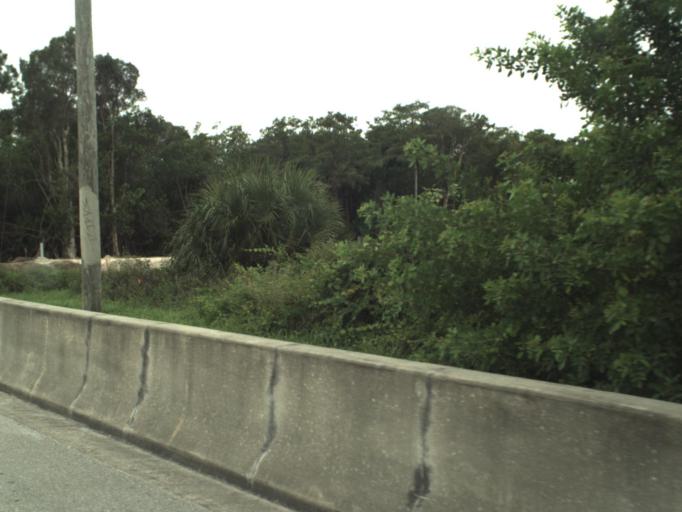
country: US
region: Florida
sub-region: Palm Beach County
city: Schall Circle
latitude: 26.7505
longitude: -80.1094
